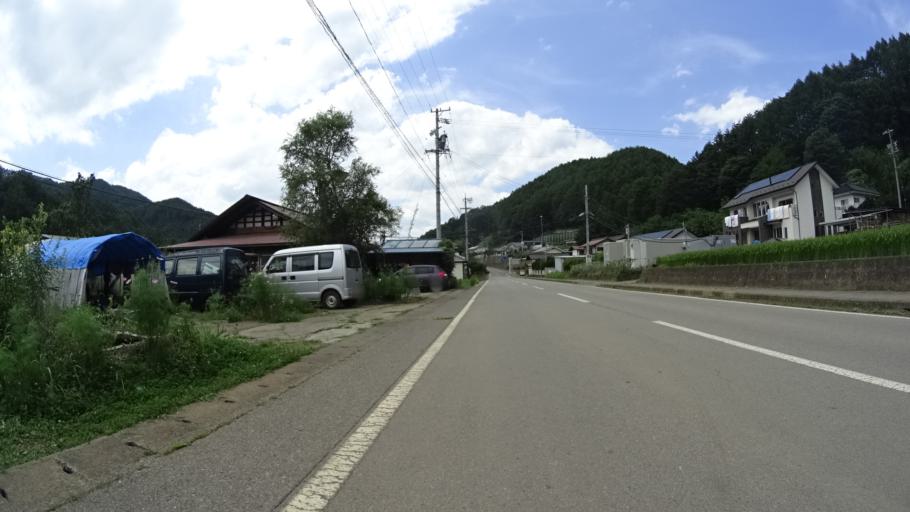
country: JP
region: Nagano
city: Saku
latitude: 36.0600
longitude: 138.5406
